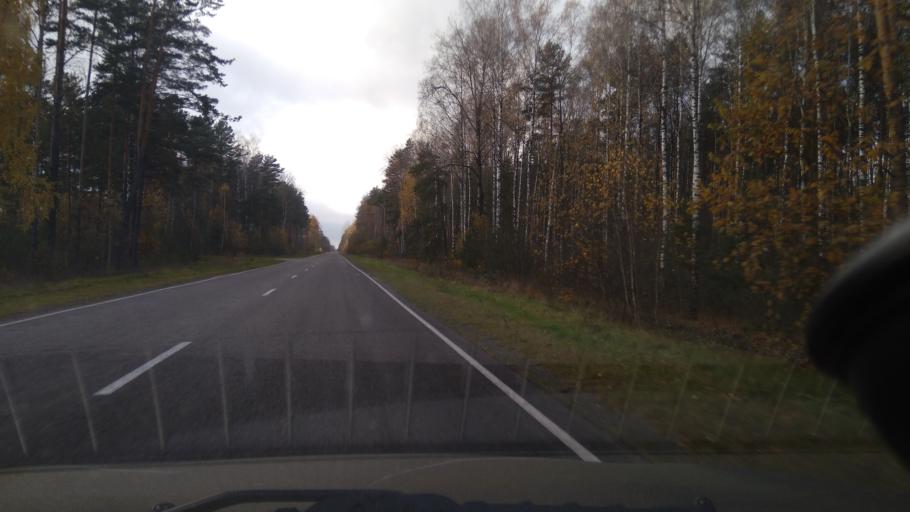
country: BY
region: Minsk
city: Urechcha
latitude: 53.2095
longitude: 27.9754
